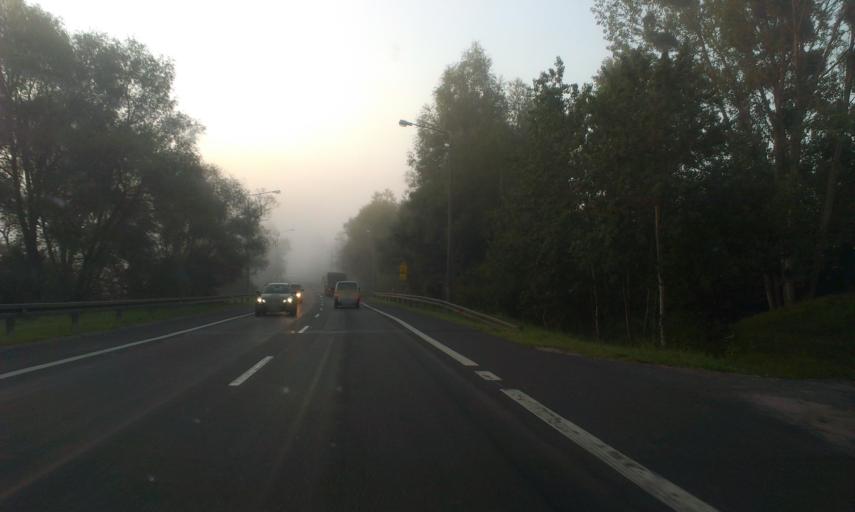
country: PL
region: Kujawsko-Pomorskie
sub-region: Powiat swiecki
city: Swiecie
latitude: 53.3939
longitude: 18.4032
